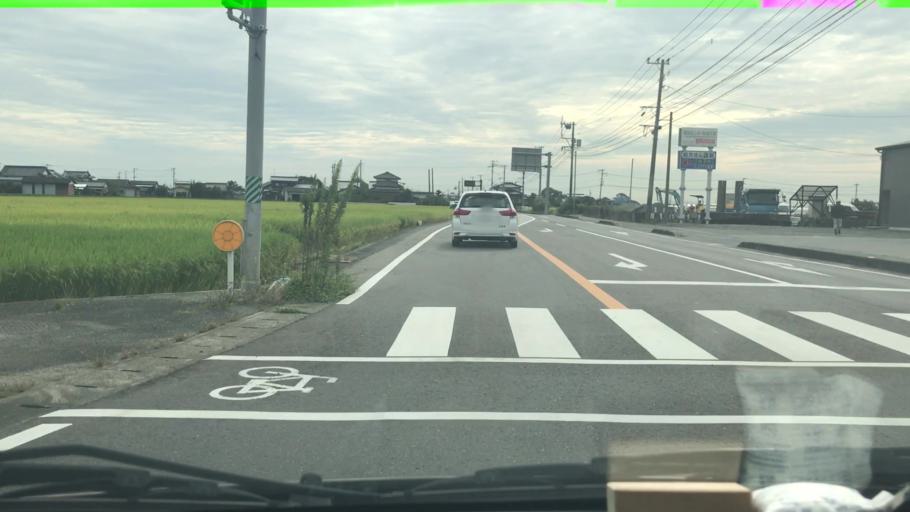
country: JP
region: Saga Prefecture
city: Takeocho-takeo
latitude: 33.1986
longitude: 130.1026
